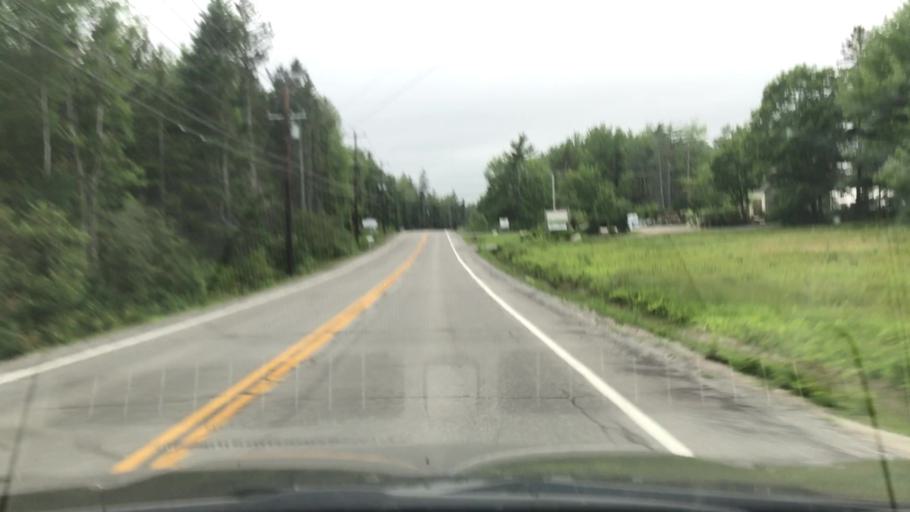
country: US
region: Maine
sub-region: Hancock County
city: Trenton
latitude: 44.4075
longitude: -68.3493
